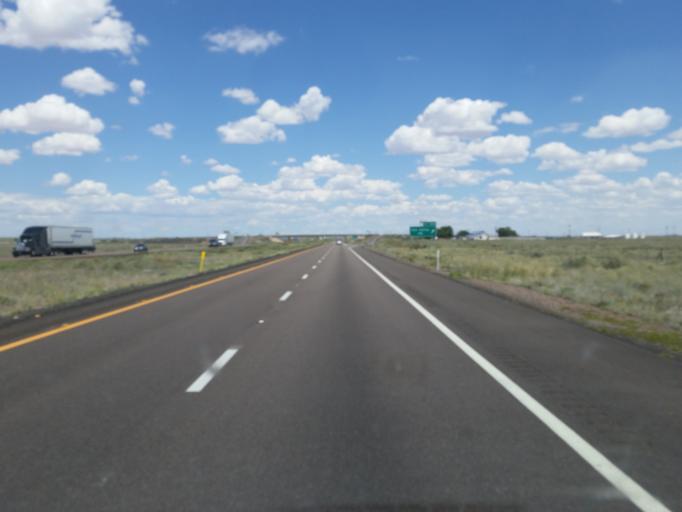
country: US
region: Arizona
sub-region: Navajo County
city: Holbrook
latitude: 34.9787
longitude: -110.0649
